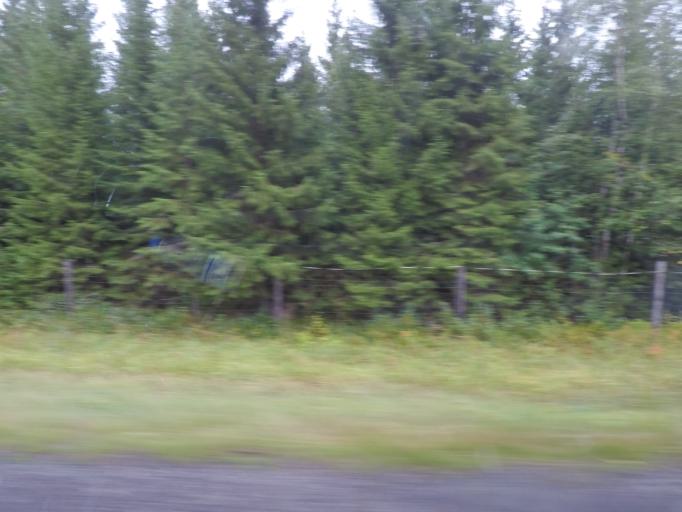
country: FI
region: Southern Savonia
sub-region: Pieksaemaeki
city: Juva
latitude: 62.0011
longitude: 27.8024
